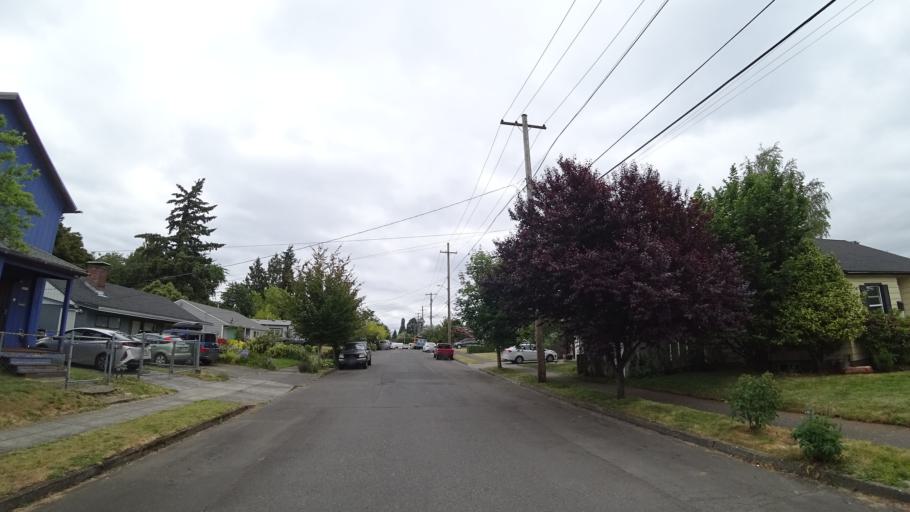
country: US
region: Oregon
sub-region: Multnomah County
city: Lents
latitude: 45.5115
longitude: -122.5811
